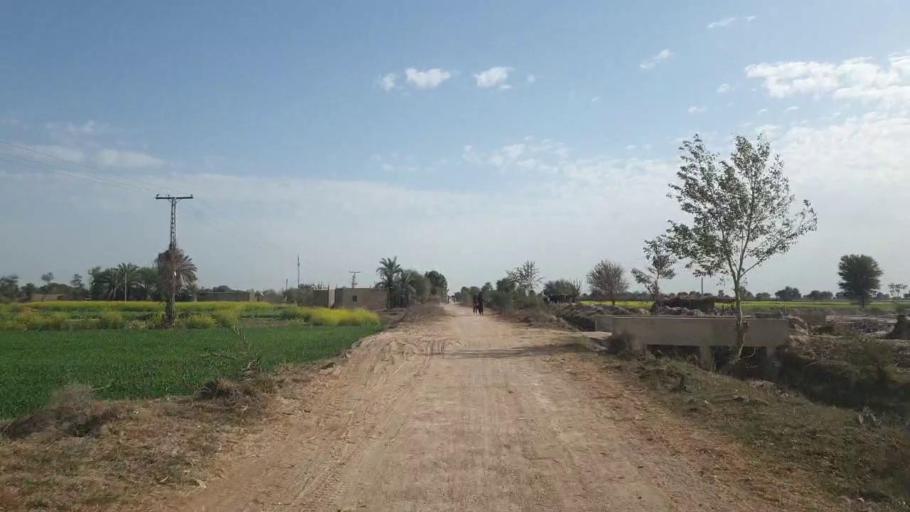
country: PK
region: Sindh
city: Shahdadpur
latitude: 26.0199
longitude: 68.4944
